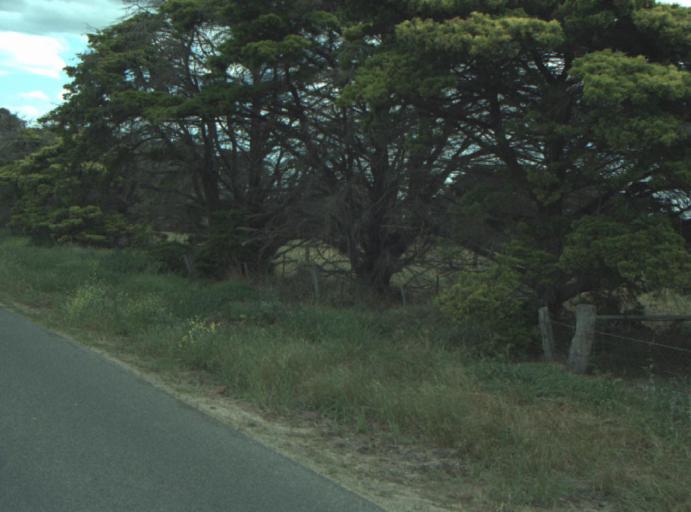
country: AU
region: Victoria
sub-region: Wyndham
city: Little River
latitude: -37.9510
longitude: 144.4652
